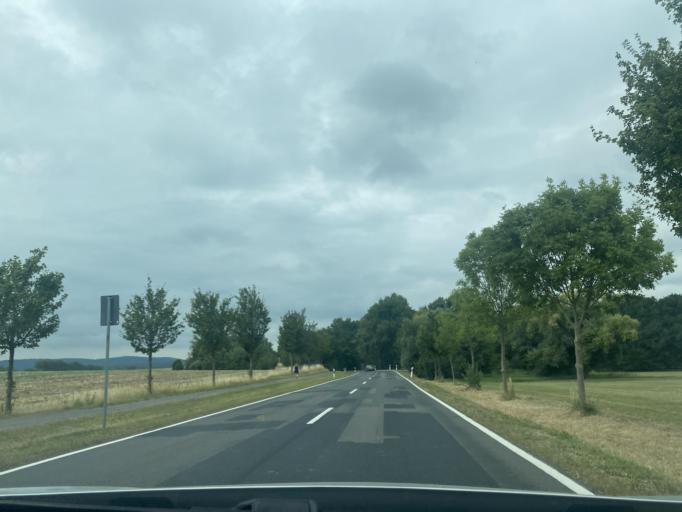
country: DE
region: Saxony
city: Quitzdorf
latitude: 51.2912
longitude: 14.7696
